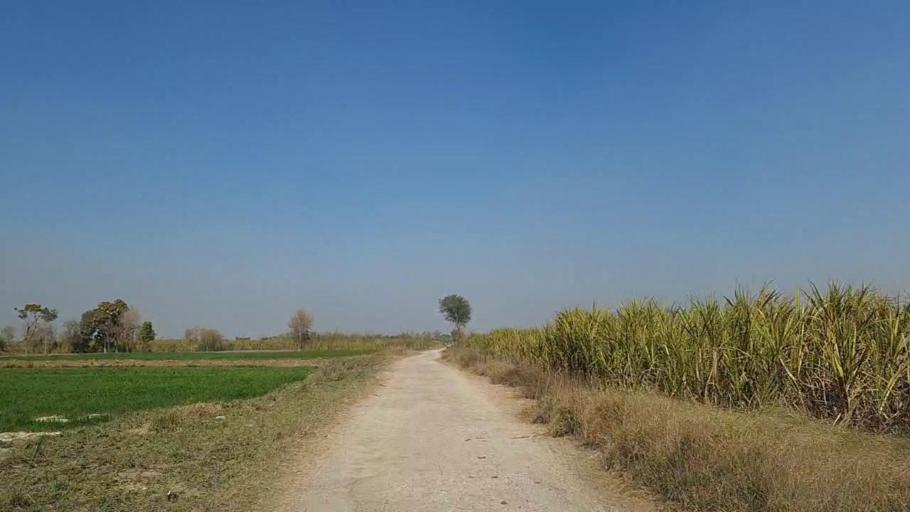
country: PK
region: Sindh
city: Daur
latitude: 26.4939
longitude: 68.3386
